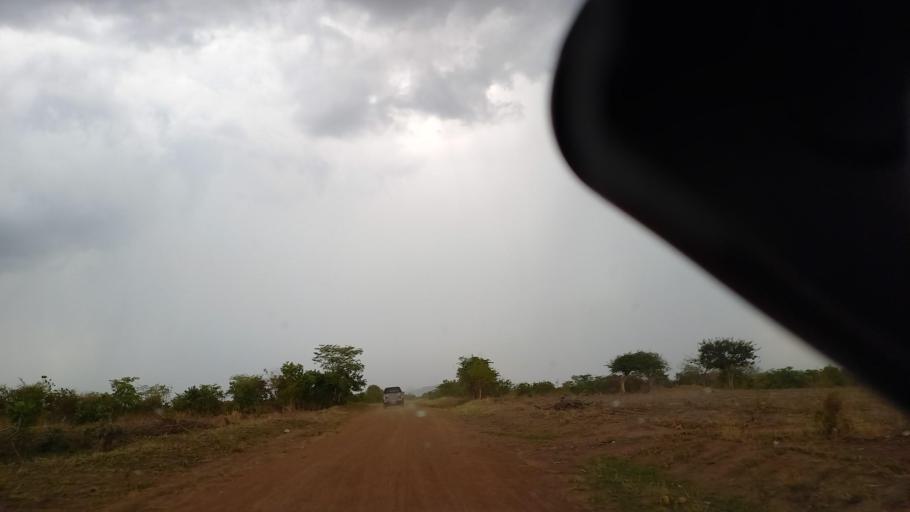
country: ZM
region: Lusaka
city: Kafue
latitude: -15.8681
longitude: 28.1927
